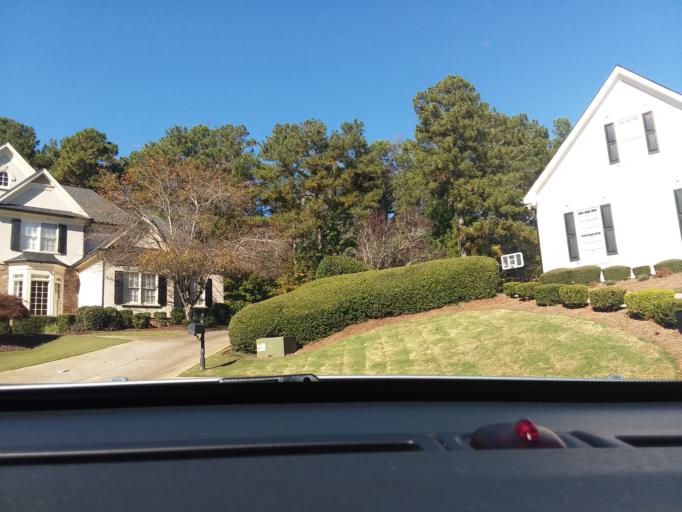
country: US
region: Georgia
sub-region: Fulton County
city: Johns Creek
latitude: 34.0274
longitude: -84.1861
